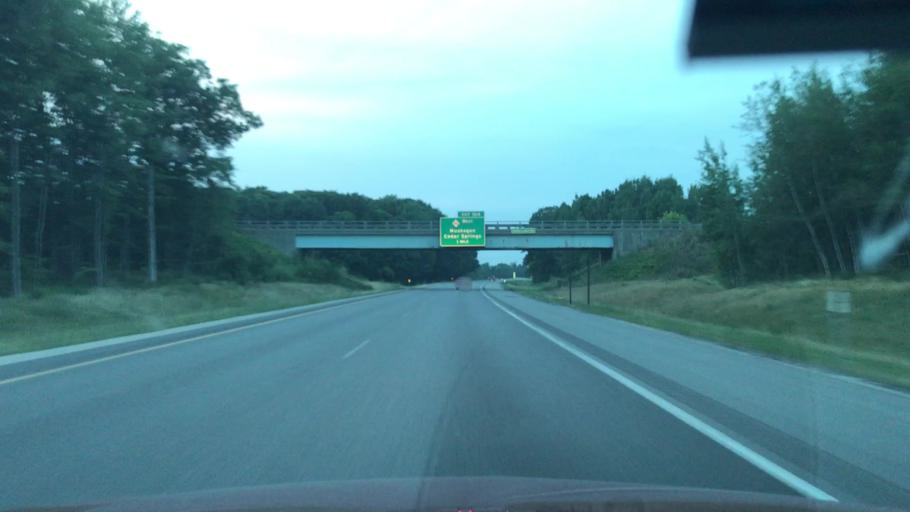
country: US
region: Michigan
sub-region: Kent County
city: Cedar Springs
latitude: 43.1965
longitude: -85.5766
